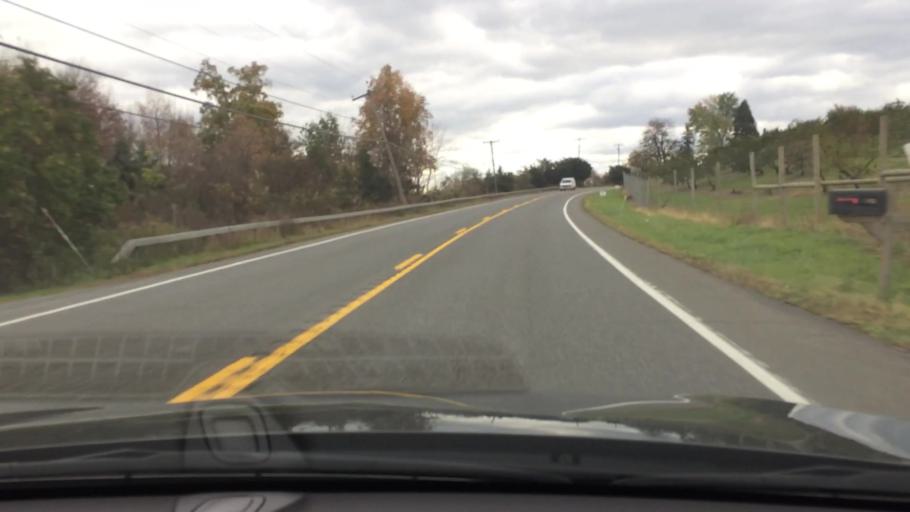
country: US
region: New York
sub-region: Columbia County
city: Stottville
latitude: 42.3144
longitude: -73.7014
